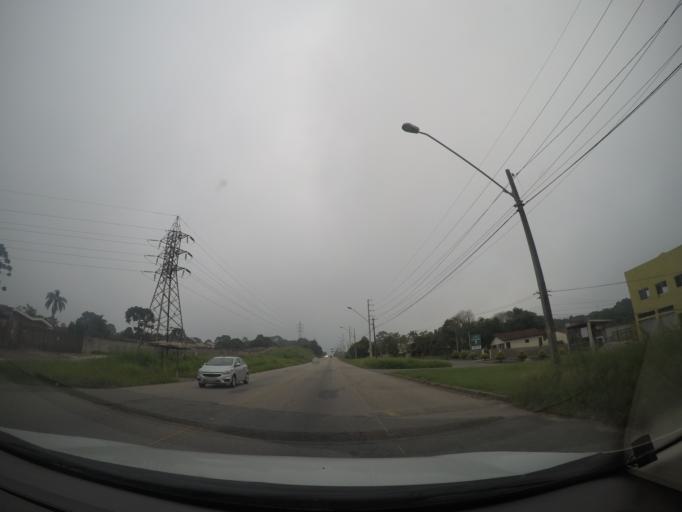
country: BR
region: Parana
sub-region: Curitiba
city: Curitiba
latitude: -25.3791
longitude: -49.2734
